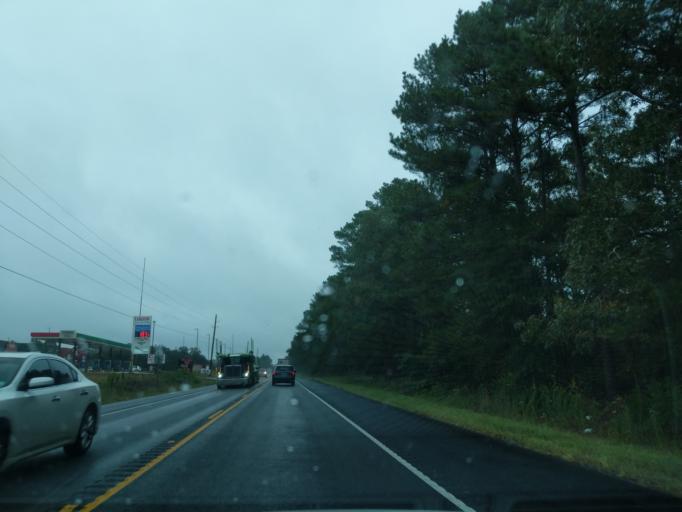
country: US
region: Louisiana
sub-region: Caddo Parish
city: Greenwood
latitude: 32.3962
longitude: -94.0059
